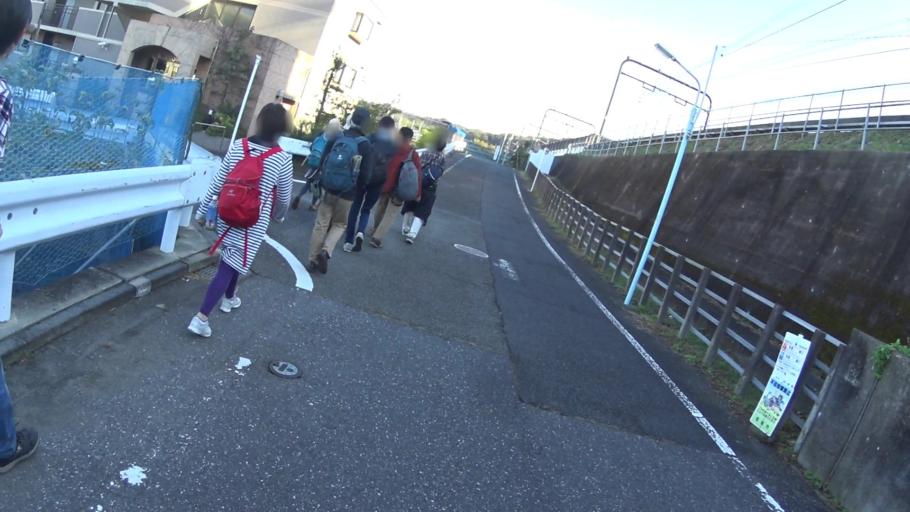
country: JP
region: Tokyo
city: Chofugaoka
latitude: 35.6356
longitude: 139.5050
